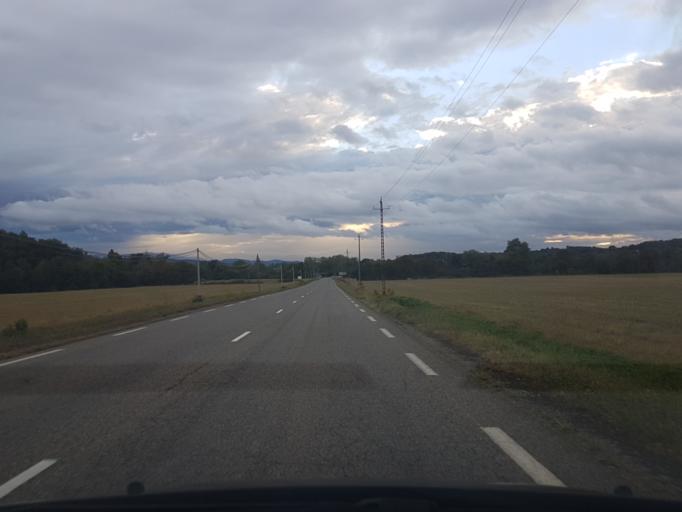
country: FR
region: Midi-Pyrenees
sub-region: Departement de l'Ariege
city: Mirepoix
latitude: 43.1019
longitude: 1.9100
